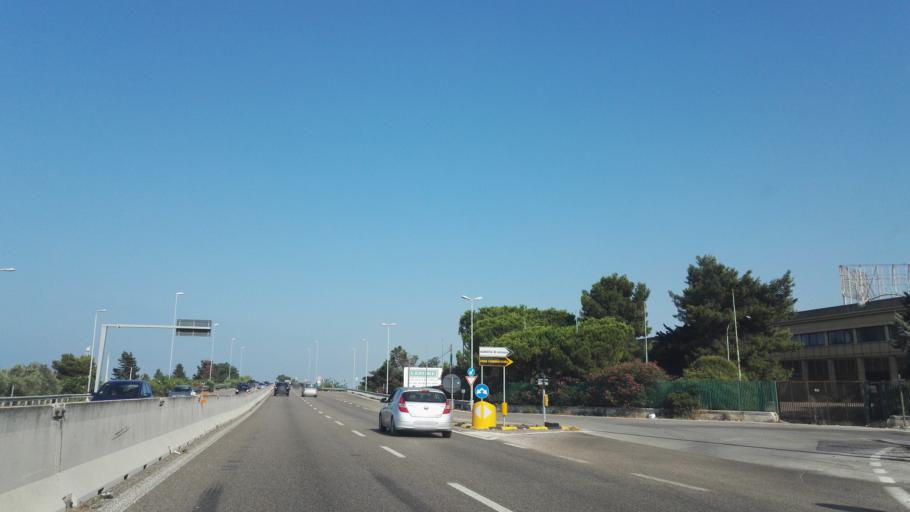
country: IT
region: Apulia
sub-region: Provincia di Bari
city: Triggiano
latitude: 41.0926
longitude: 16.9561
